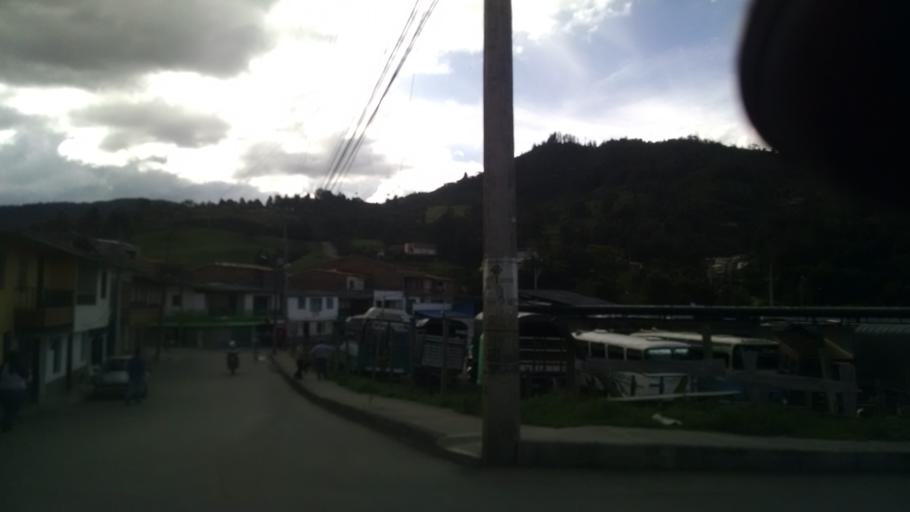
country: CO
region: Antioquia
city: El Retiro
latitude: 6.0605
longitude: -75.5034
